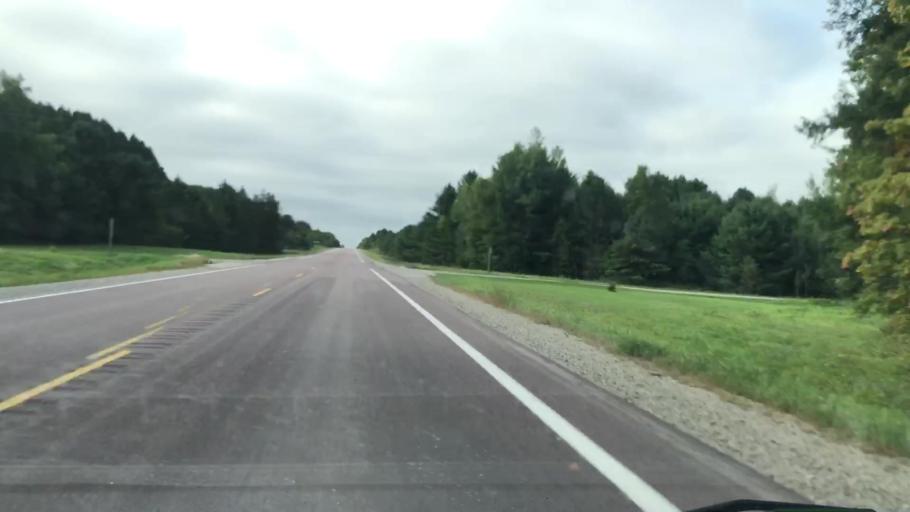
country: US
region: Michigan
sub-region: Luce County
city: Newberry
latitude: 46.2895
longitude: -85.5700
